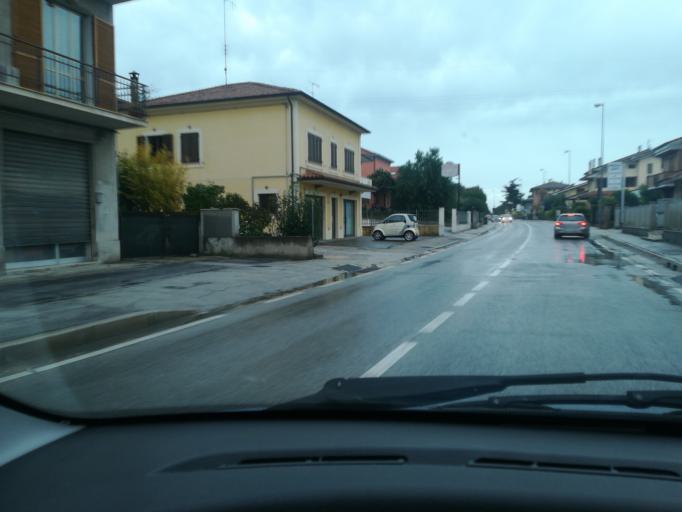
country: IT
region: The Marches
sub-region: Provincia di Macerata
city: Santa Maria Apparente
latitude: 43.2972
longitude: 13.6948
